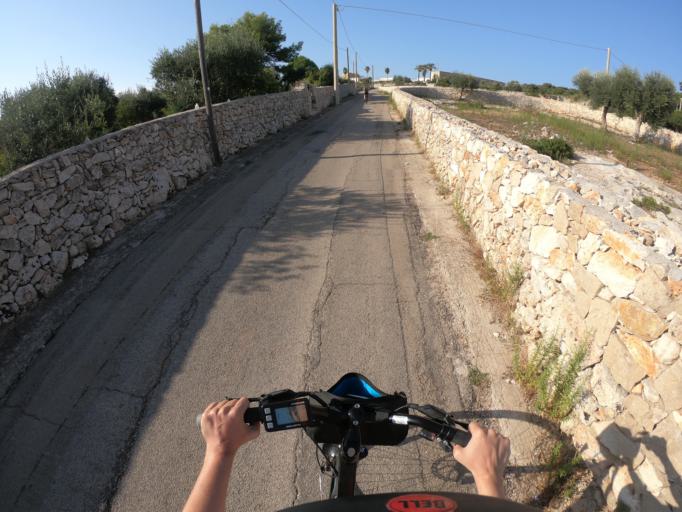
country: IT
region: Apulia
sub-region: Provincia di Lecce
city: Leuca
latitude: 39.8018
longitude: 18.3634
